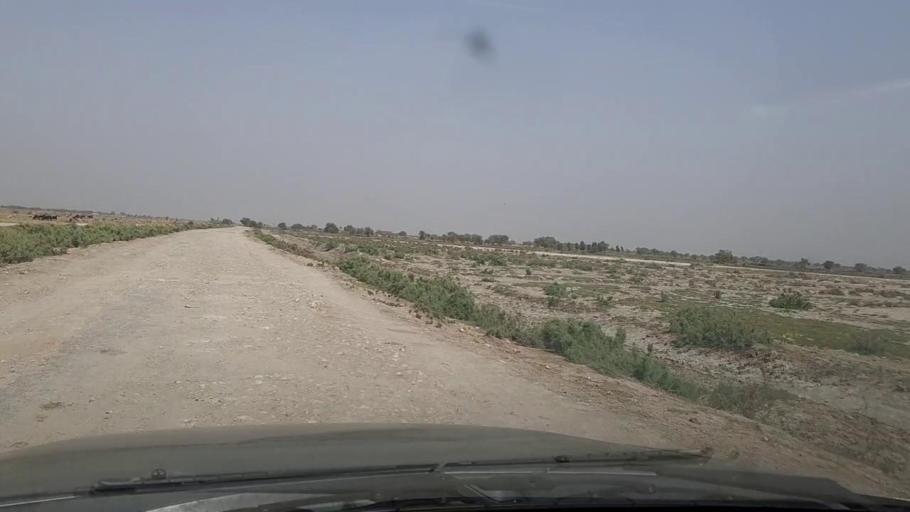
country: PK
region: Sindh
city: Thul
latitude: 28.4054
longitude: 68.7026
